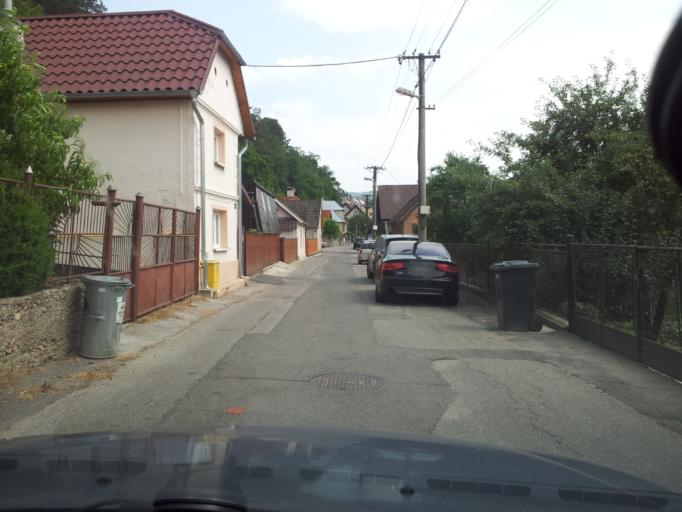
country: SK
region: Trenciansky
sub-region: Okres Trencin
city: Trencin
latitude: 48.8942
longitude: 18.0867
